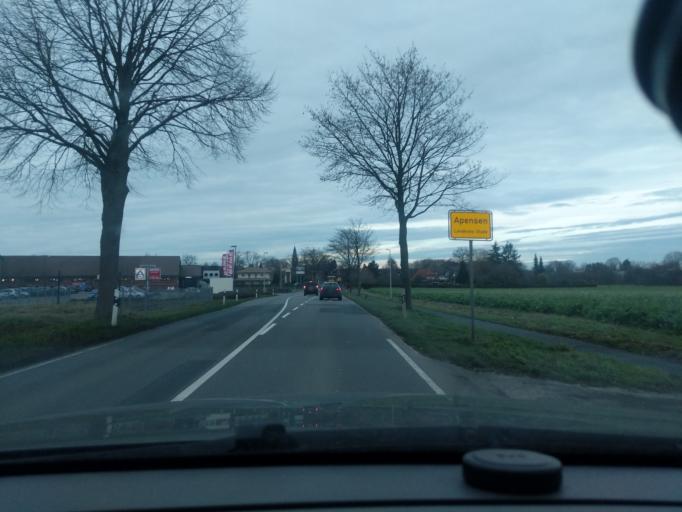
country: DE
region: Lower Saxony
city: Apensen
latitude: 53.4295
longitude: 9.6134
